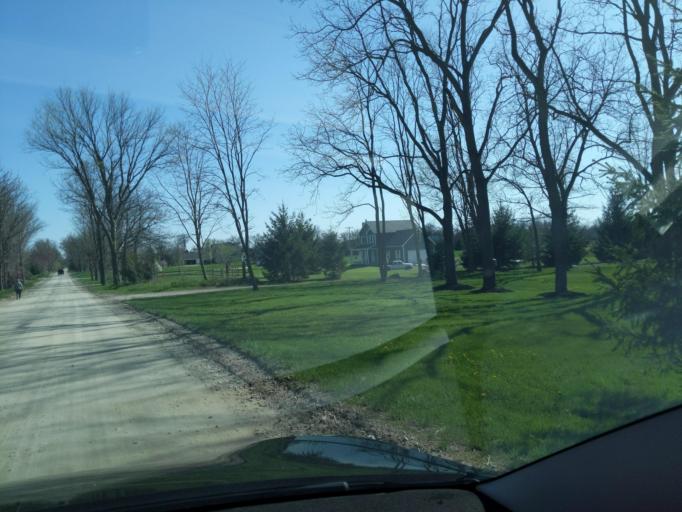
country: US
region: Michigan
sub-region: Ingham County
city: Stockbridge
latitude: 42.4208
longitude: -84.0836
